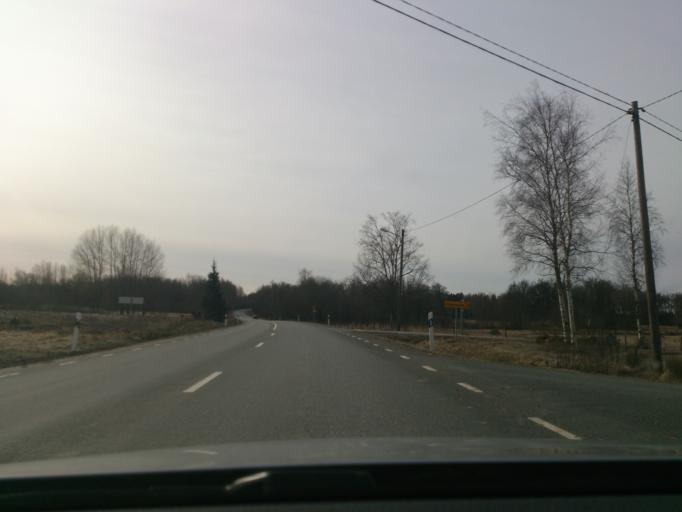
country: SE
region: Kronoberg
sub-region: Alvesta Kommun
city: Alvesta
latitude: 56.9333
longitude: 14.5587
